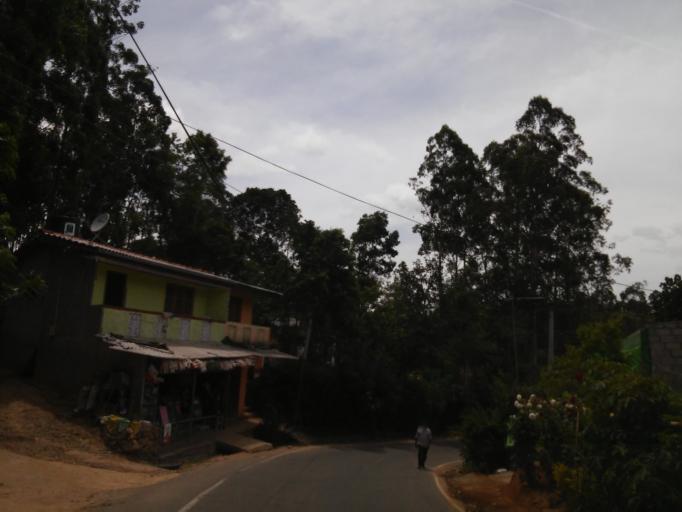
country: LK
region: Uva
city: Haputale
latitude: 6.8503
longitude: 81.0266
